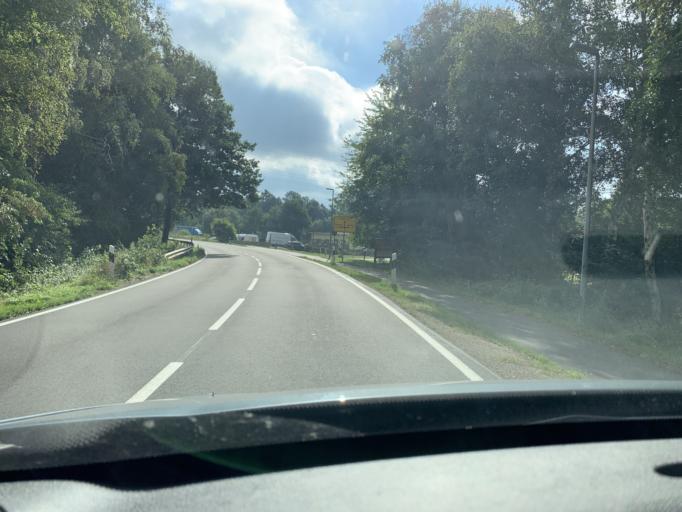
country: DE
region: Lower Saxony
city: Edewecht
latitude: 53.0978
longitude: 8.0872
